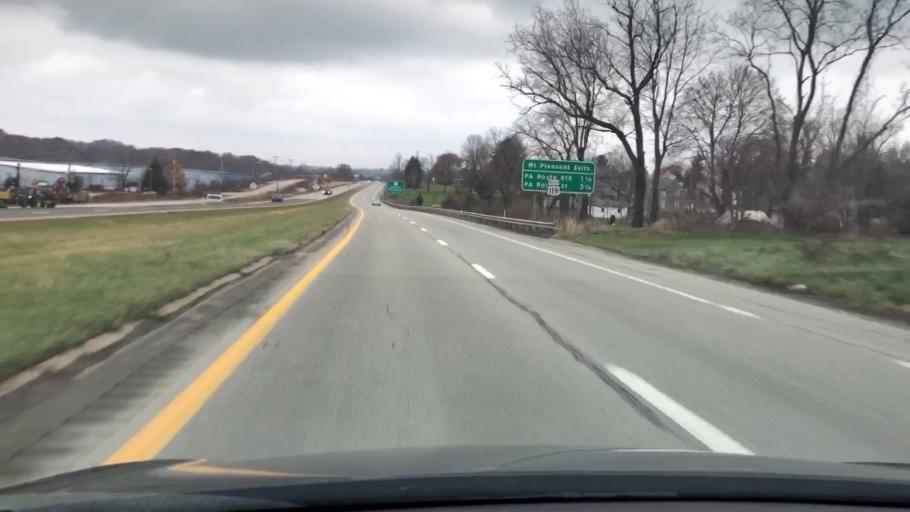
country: US
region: Pennsylvania
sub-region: Westmoreland County
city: Scottdale
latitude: 40.1051
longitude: -79.5558
